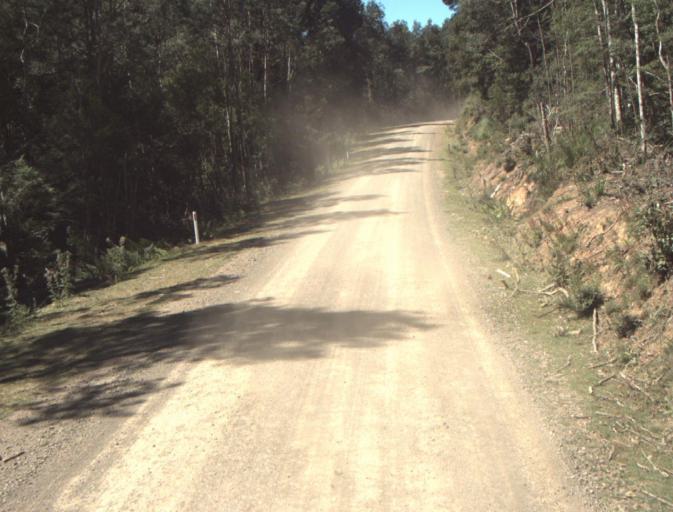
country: AU
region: Tasmania
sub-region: Dorset
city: Scottsdale
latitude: -41.3793
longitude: 147.4835
